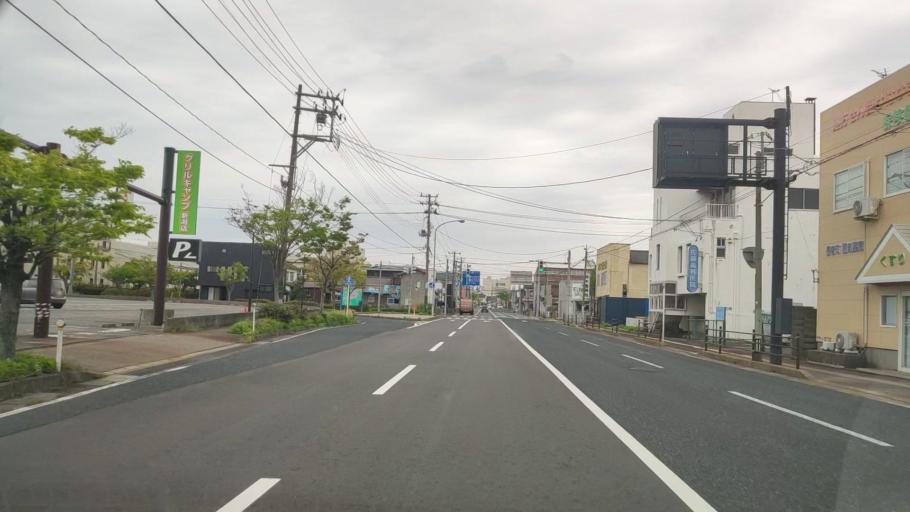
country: JP
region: Niigata
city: Niigata-shi
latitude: 37.9355
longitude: 139.0724
